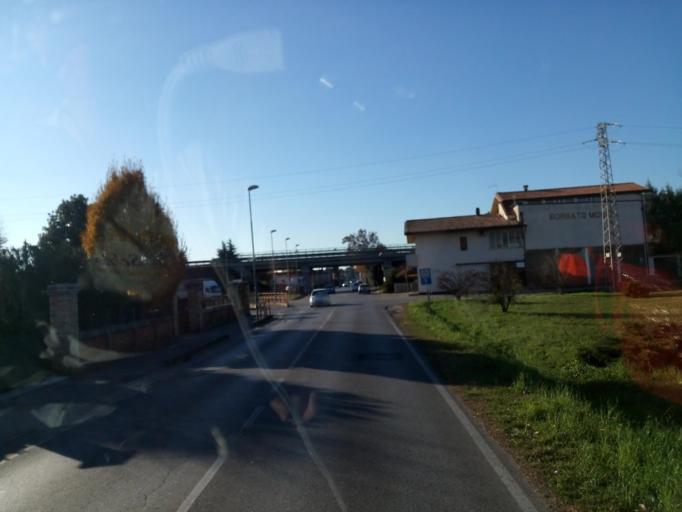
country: IT
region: Veneto
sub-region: Provincia di Treviso
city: Montebelluna
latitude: 45.7806
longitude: 12.0688
